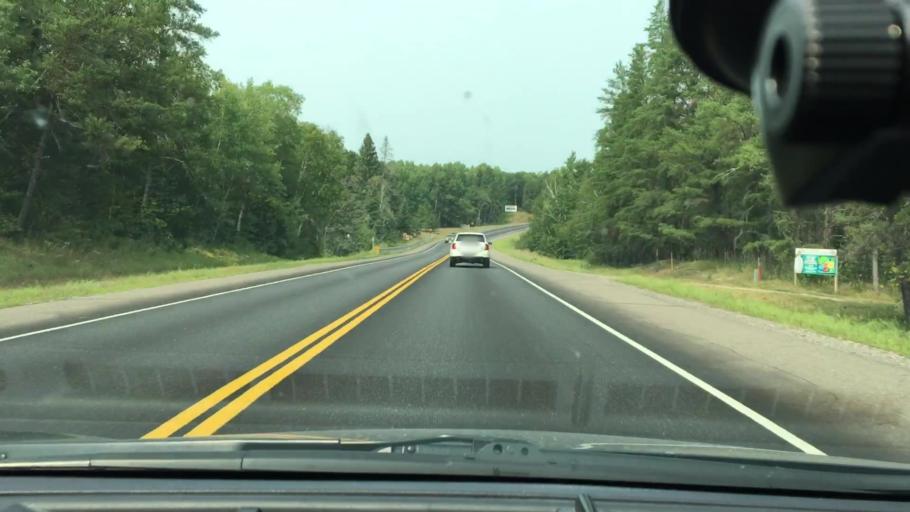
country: US
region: Minnesota
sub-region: Crow Wing County
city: Cross Lake
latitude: 46.6245
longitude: -94.1317
